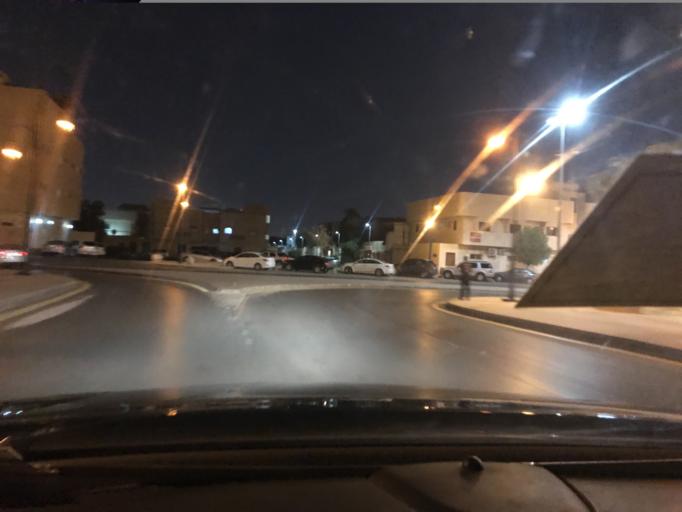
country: SA
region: Ar Riyad
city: Riyadh
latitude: 24.7415
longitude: 46.7693
